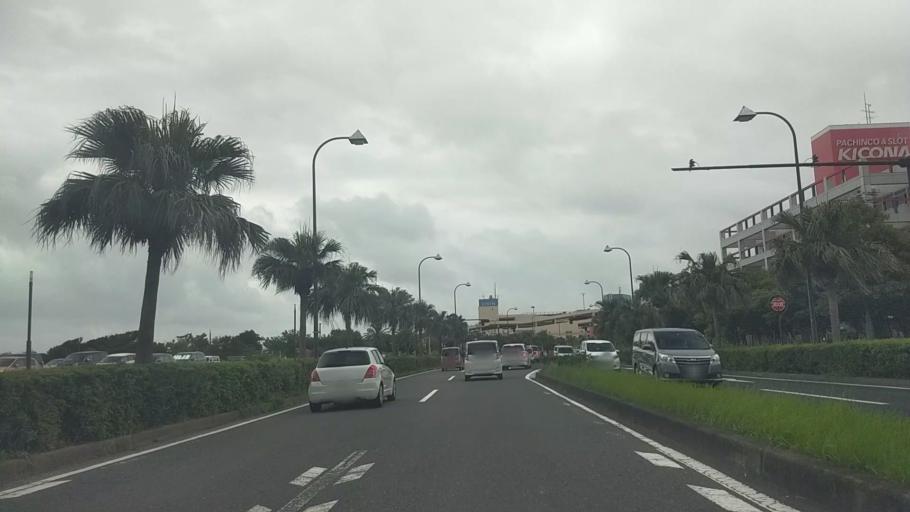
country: JP
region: Kanagawa
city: Yokosuka
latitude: 35.2776
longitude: 139.6804
